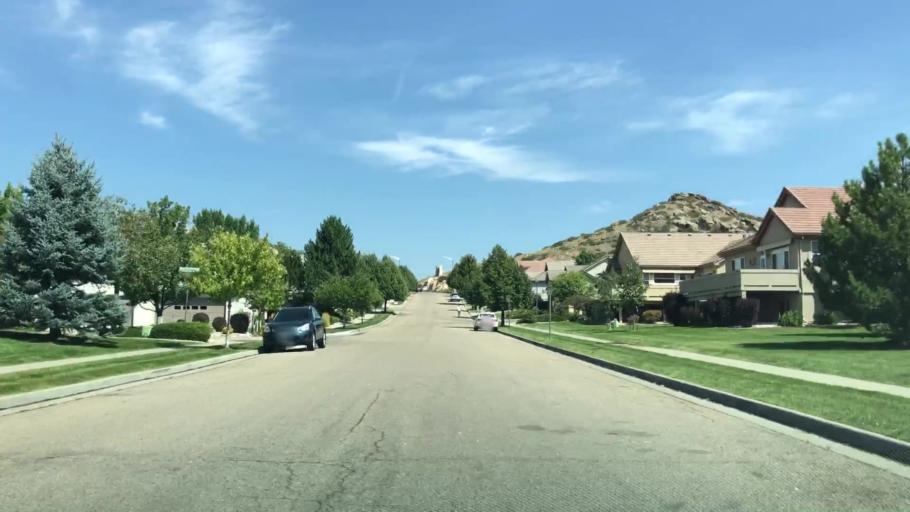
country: US
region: Colorado
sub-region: Larimer County
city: Loveland
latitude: 40.3962
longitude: -105.1431
